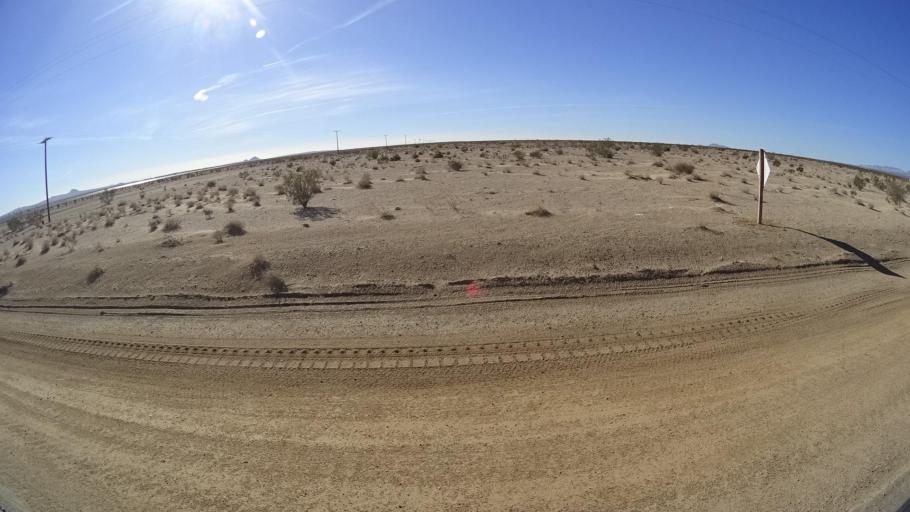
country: US
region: California
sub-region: Kern County
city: California City
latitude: 35.1987
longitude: -118.0043
